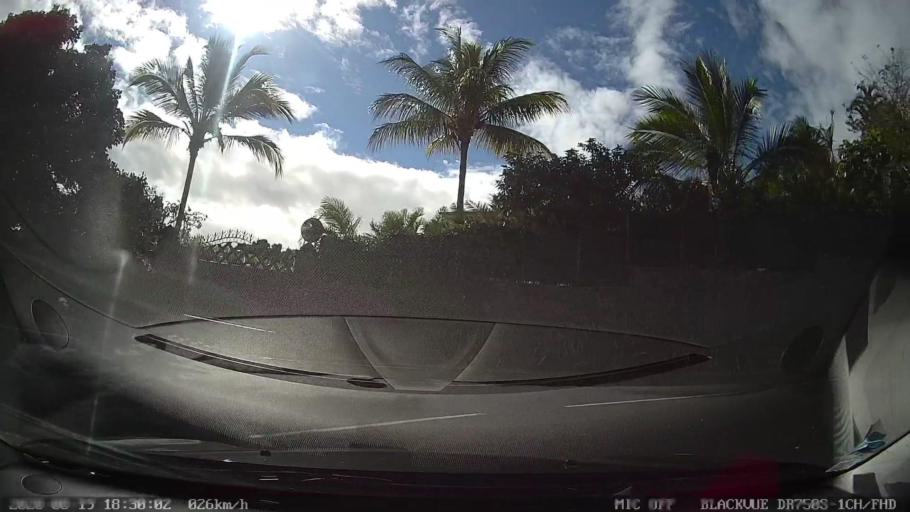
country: RE
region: Reunion
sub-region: Reunion
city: La Possession
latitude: -20.9586
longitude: 55.3492
